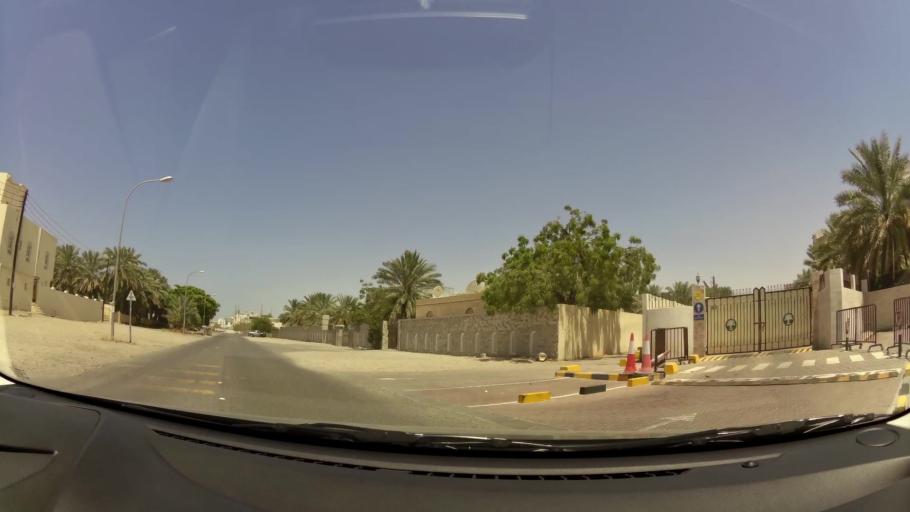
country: OM
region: Muhafazat Masqat
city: As Sib al Jadidah
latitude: 23.6178
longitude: 58.2302
